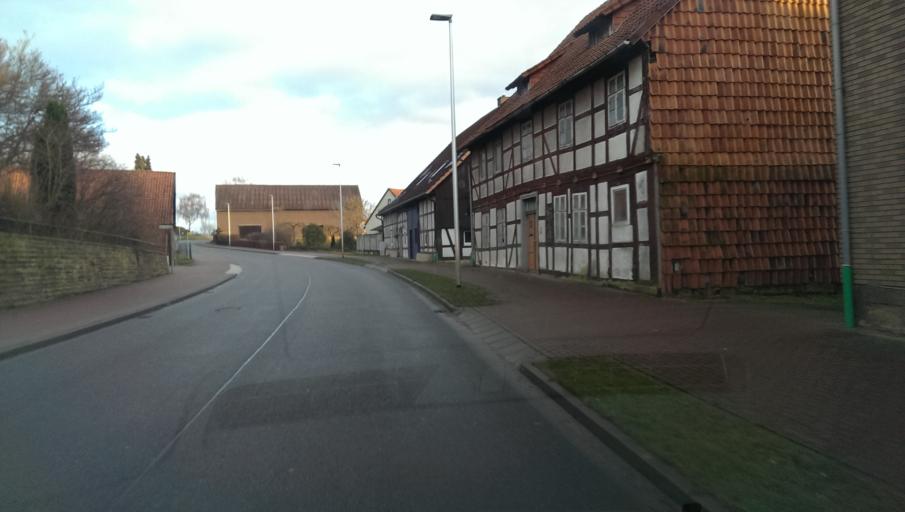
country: DE
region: Lower Saxony
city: Eimen
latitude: 51.8701
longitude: 9.8138
